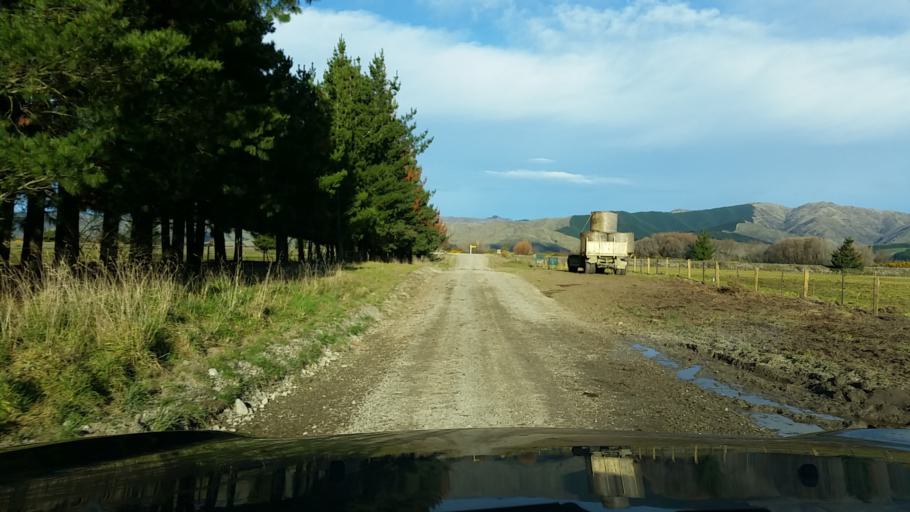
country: NZ
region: Nelson
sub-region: Nelson City
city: Nelson
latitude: -41.5679
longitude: 173.4517
